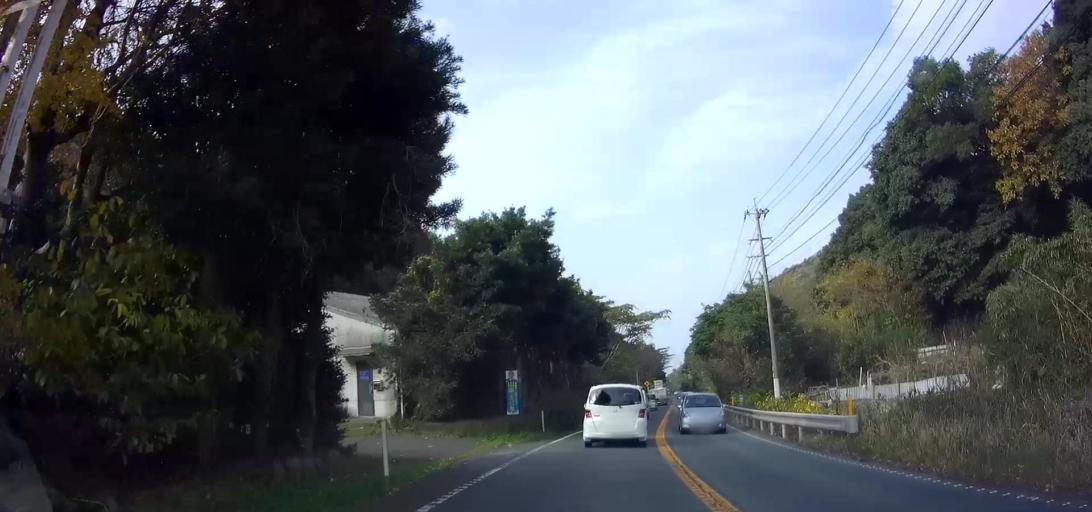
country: JP
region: Nagasaki
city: Shimabara
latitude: 32.7614
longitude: 130.2085
